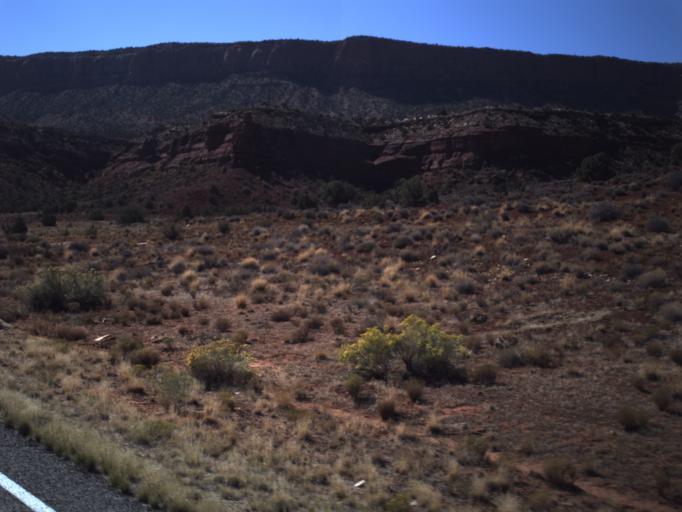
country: US
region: Utah
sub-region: San Juan County
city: Blanding
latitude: 37.6962
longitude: -110.2308
